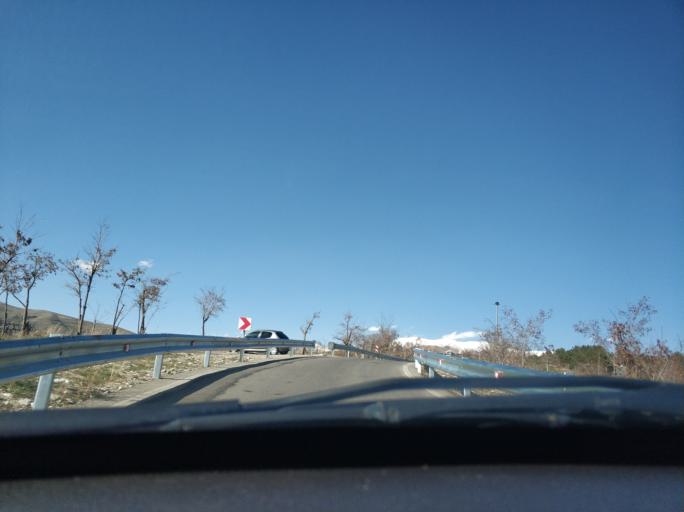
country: IR
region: Tehran
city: Tajrish
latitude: 35.7956
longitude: 51.5621
